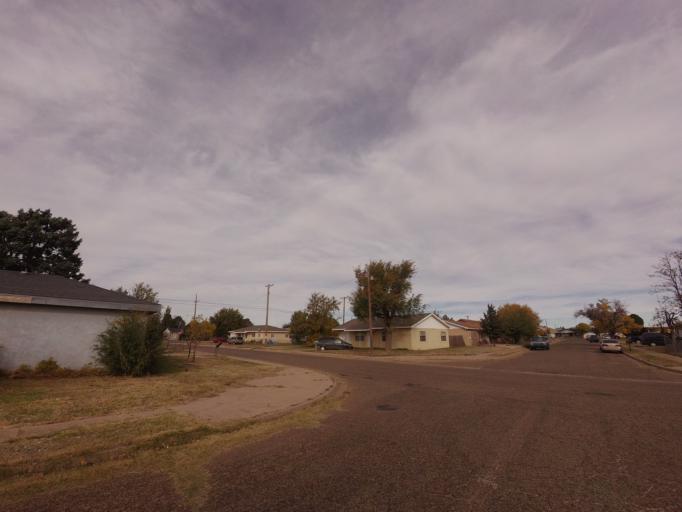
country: US
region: New Mexico
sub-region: Curry County
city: Clovis
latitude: 34.4285
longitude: -103.2131
